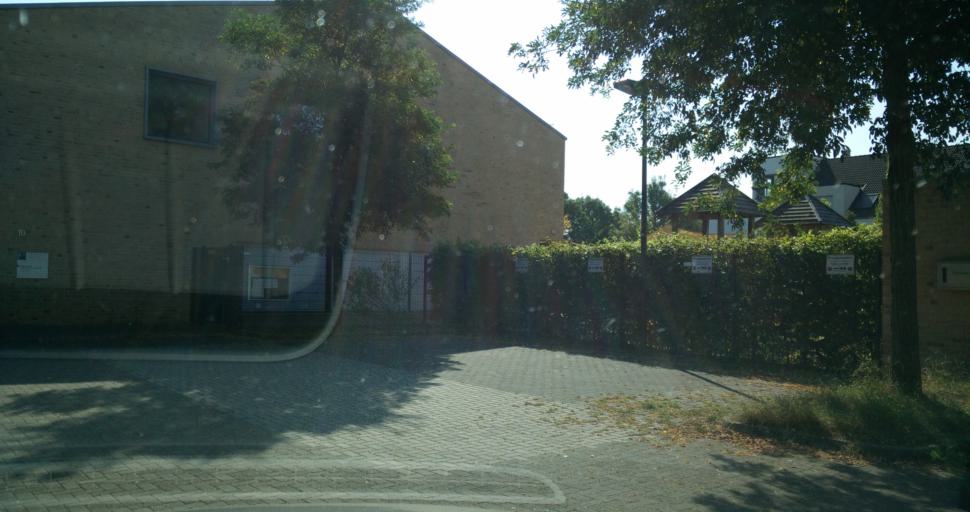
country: DE
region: North Rhine-Westphalia
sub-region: Regierungsbezirk Dusseldorf
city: Meerbusch
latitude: 51.3198
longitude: 6.7448
